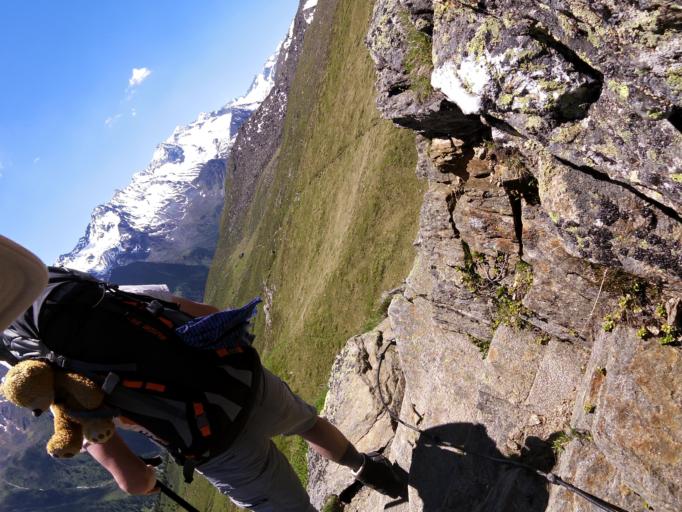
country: AT
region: Tyrol
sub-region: Politischer Bezirk Innsbruck Land
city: Gries im Sellrain
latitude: 47.1213
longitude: 11.2144
